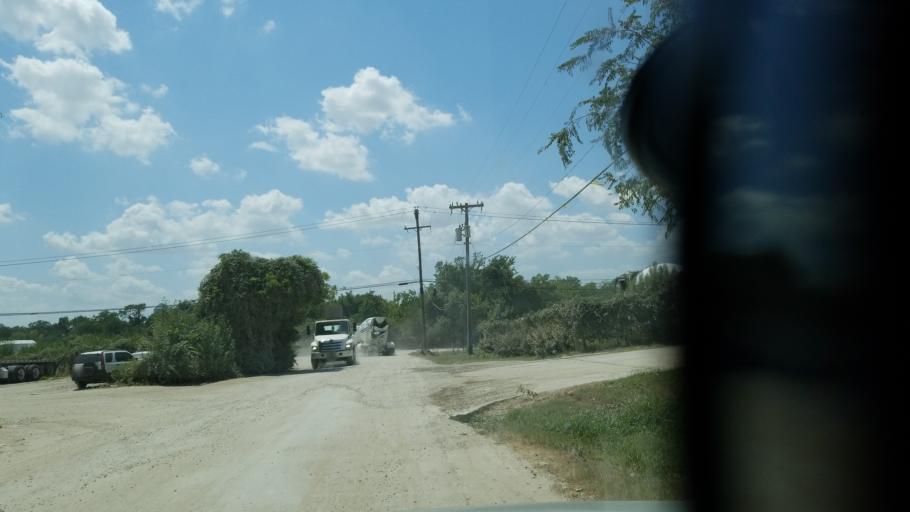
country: US
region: Texas
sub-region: Dallas County
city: Farmers Branch
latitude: 32.8761
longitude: -96.9190
